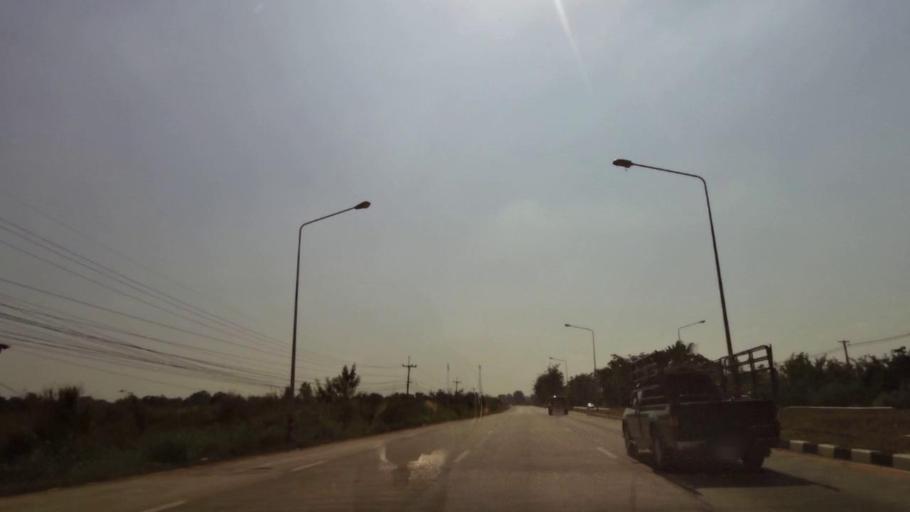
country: TH
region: Phichit
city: Wachira Barami
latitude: 16.3526
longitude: 100.1290
